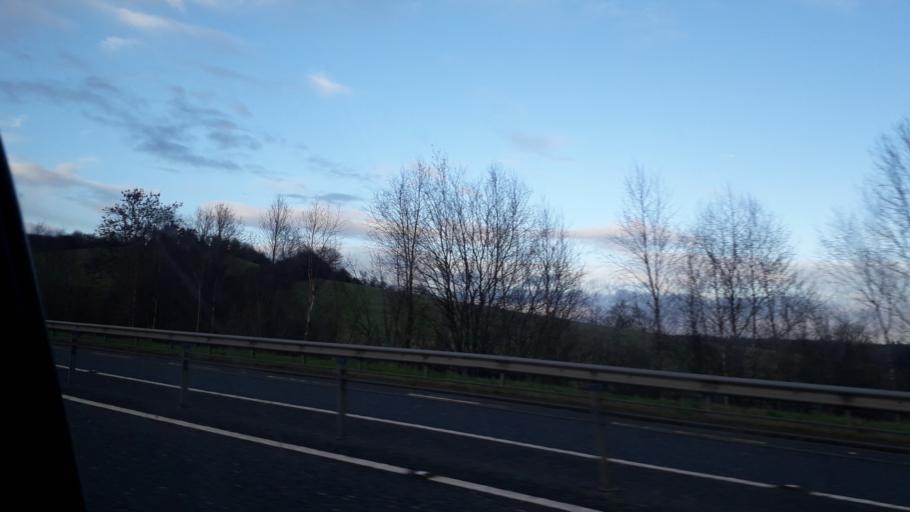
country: IE
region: Ulster
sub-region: County Monaghan
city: Castleblayney
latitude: 54.1649
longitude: -6.8077
